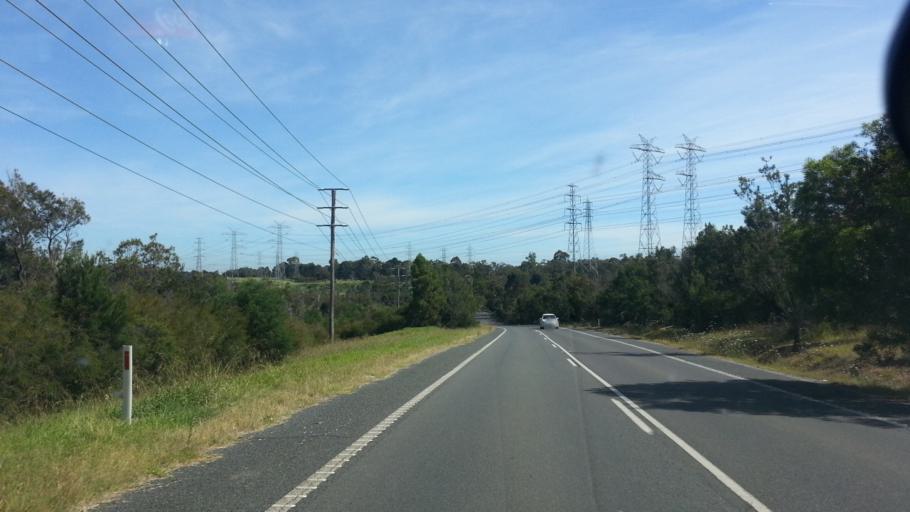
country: AU
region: Victoria
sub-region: Knox
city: Rowville
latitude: -37.9475
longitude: 145.2448
